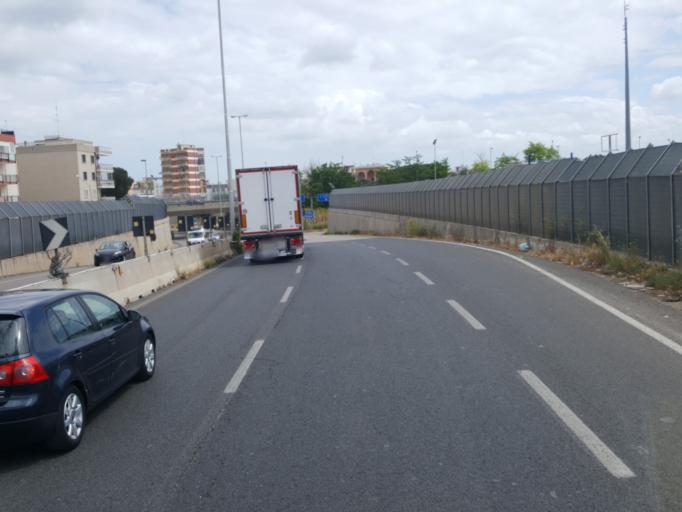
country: IT
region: Apulia
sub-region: Provincia di Bari
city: Modugno
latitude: 41.0873
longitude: 16.7719
